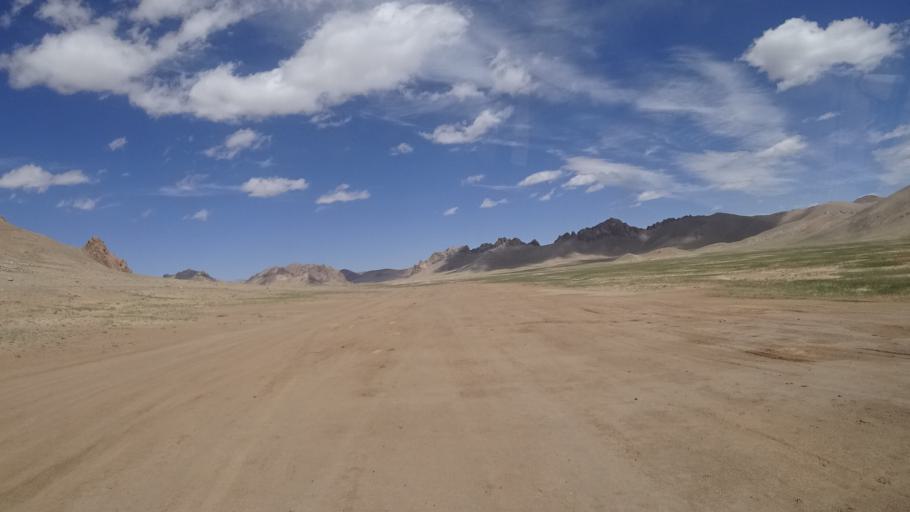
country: TJ
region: Gorno-Badakhshan
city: Murghob
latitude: 37.7727
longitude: 74.1998
